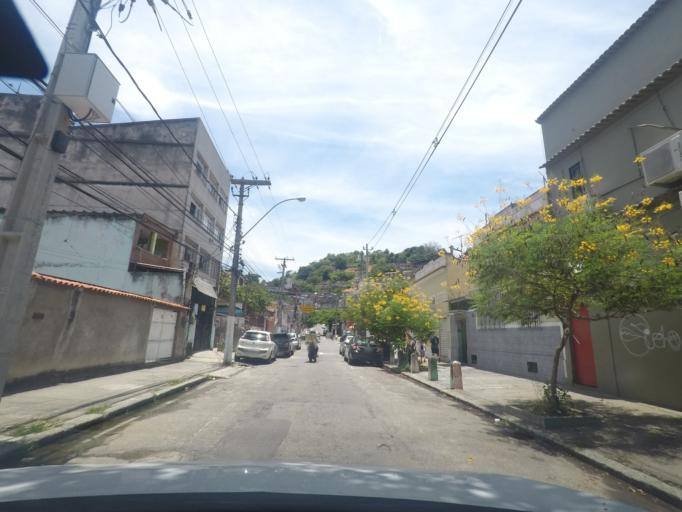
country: BR
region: Rio de Janeiro
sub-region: Niteroi
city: Niteroi
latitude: -22.8964
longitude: -43.1199
